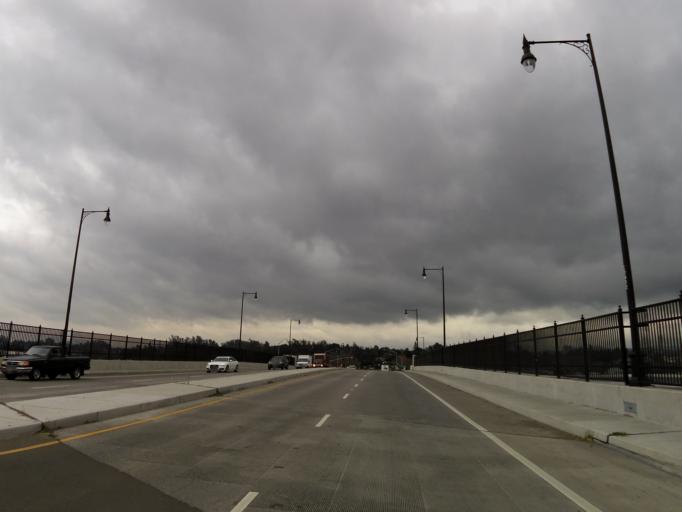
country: US
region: California
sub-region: Sonoma County
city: Penngrove
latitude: 38.2727
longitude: -122.6699
